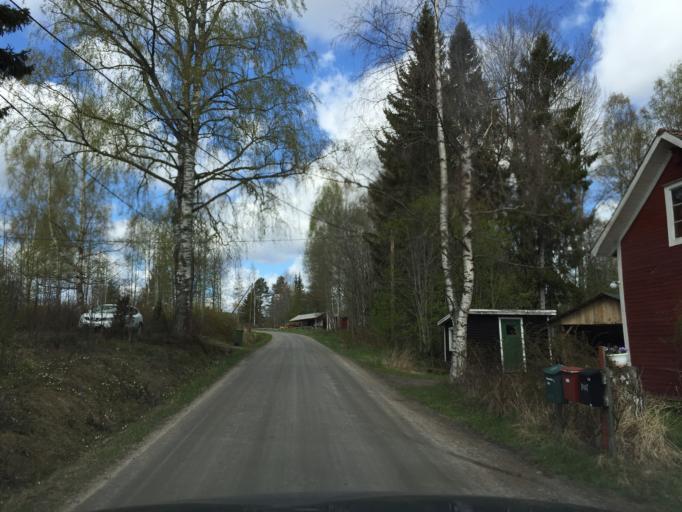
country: SE
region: Gaevleborg
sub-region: Bollnas Kommun
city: Arbra
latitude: 61.5197
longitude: 16.3481
